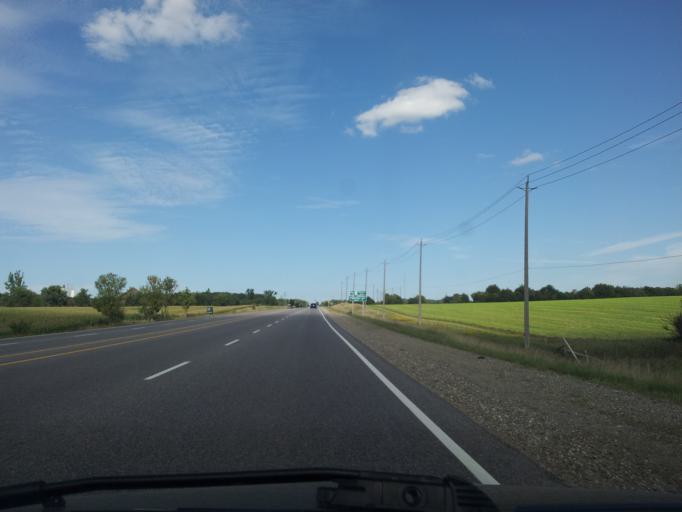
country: CA
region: Ontario
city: Kitchener
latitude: 43.3826
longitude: -80.6877
